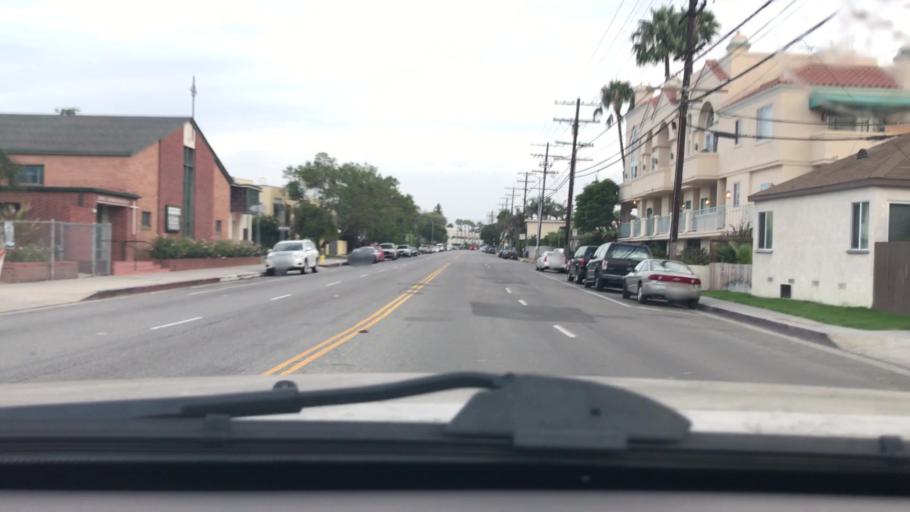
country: US
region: California
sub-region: Los Angeles County
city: Culver City
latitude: 33.9952
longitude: -118.4182
